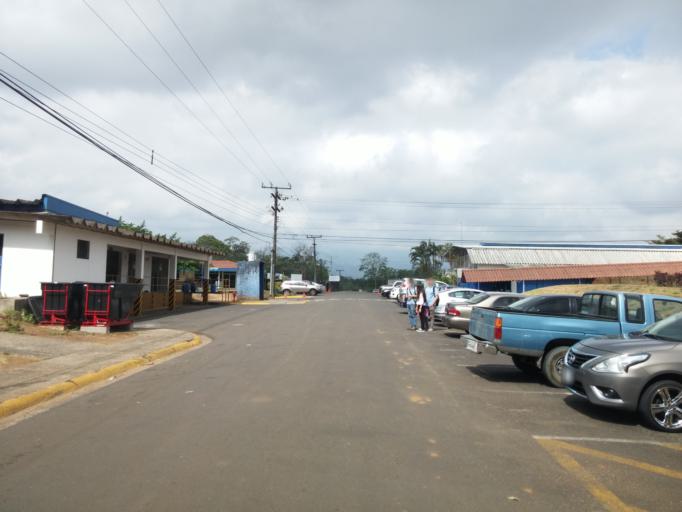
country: CR
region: Alajuela
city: Quesada
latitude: 10.3624
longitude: -84.5100
